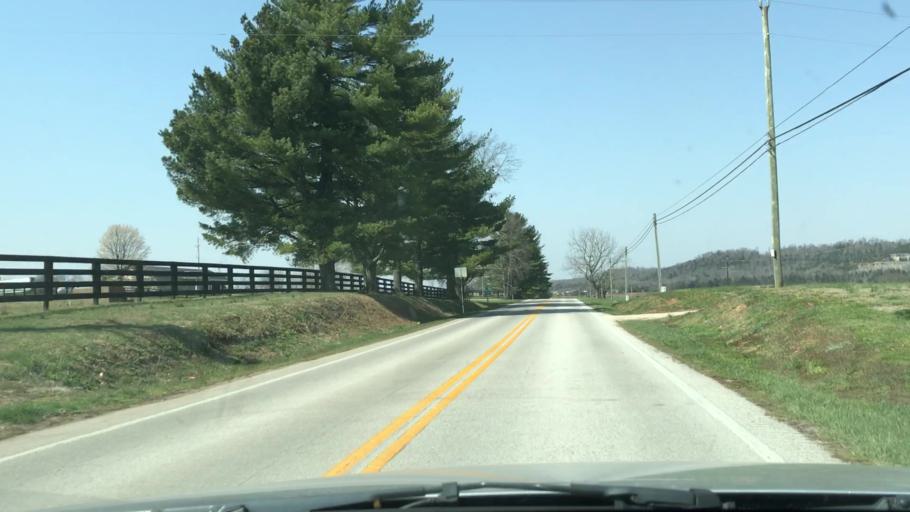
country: US
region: Kentucky
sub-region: Barren County
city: Cave City
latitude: 37.0929
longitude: -86.1030
